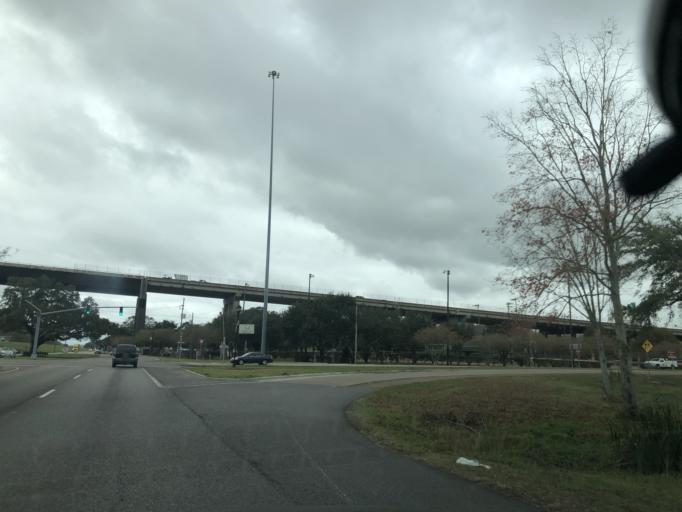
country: US
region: Louisiana
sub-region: Saint Charles Parish
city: Luling
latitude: 29.9468
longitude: -90.3692
